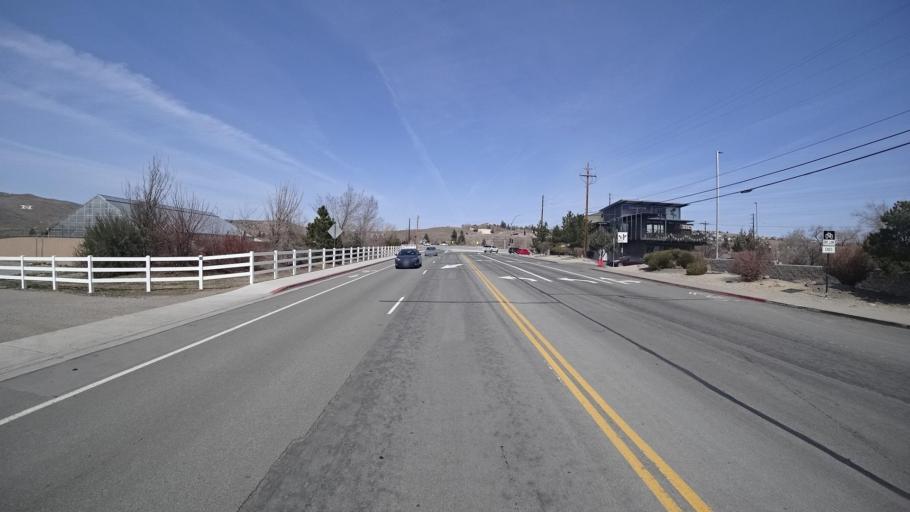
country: US
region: Nevada
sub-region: Washoe County
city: Reno
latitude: 39.5486
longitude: -119.8223
